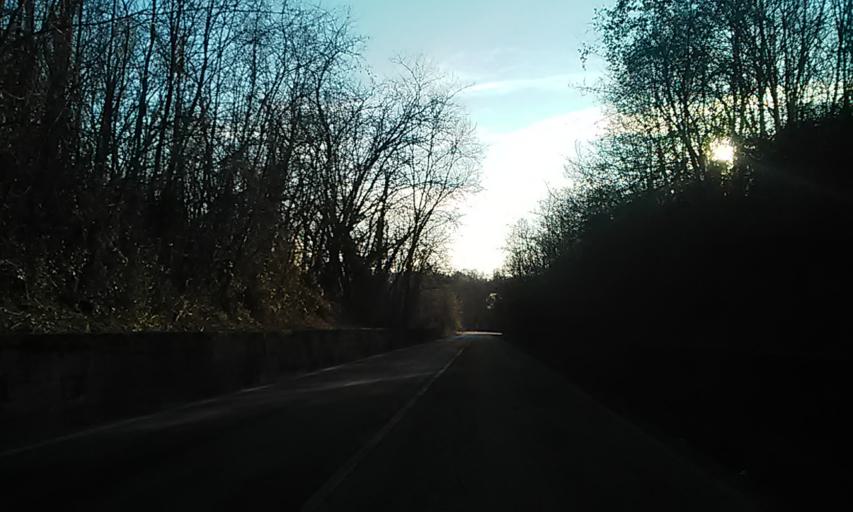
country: IT
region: Piedmont
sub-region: Provincia di Biella
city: Cossato
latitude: 45.5672
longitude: 8.2092
